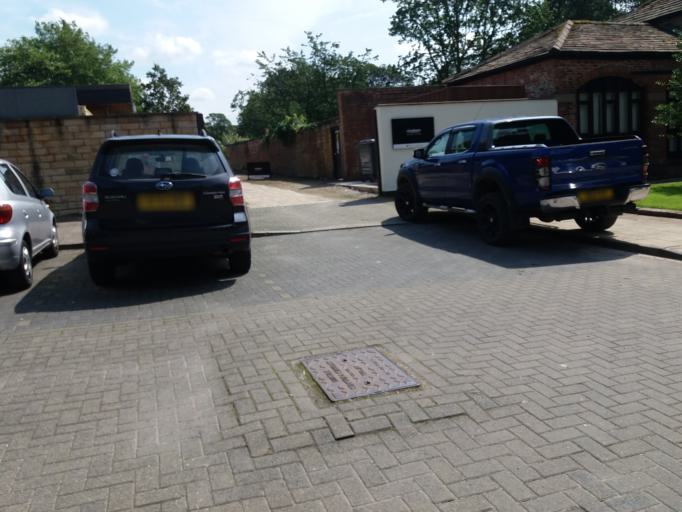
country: GB
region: England
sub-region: Lancashire
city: Chorley
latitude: 53.6310
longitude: -2.6253
